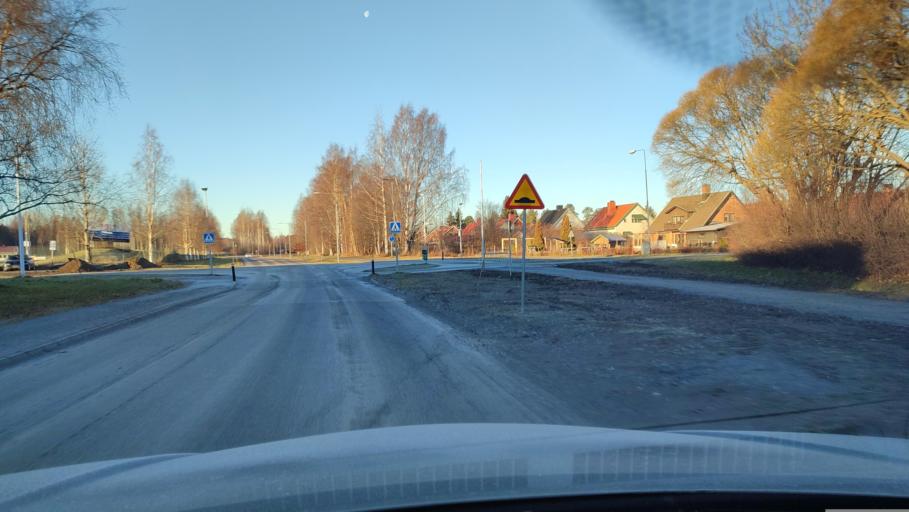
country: SE
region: Vaesterbotten
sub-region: Skelleftea Kommun
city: Skelleftea
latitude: 64.7403
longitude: 20.9485
